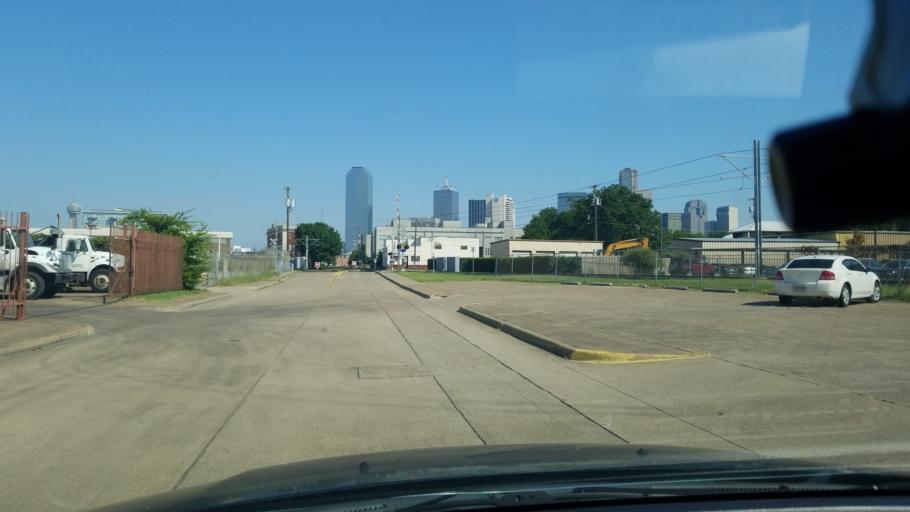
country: US
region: Texas
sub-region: Dallas County
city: Dallas
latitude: 32.7664
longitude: -96.7901
